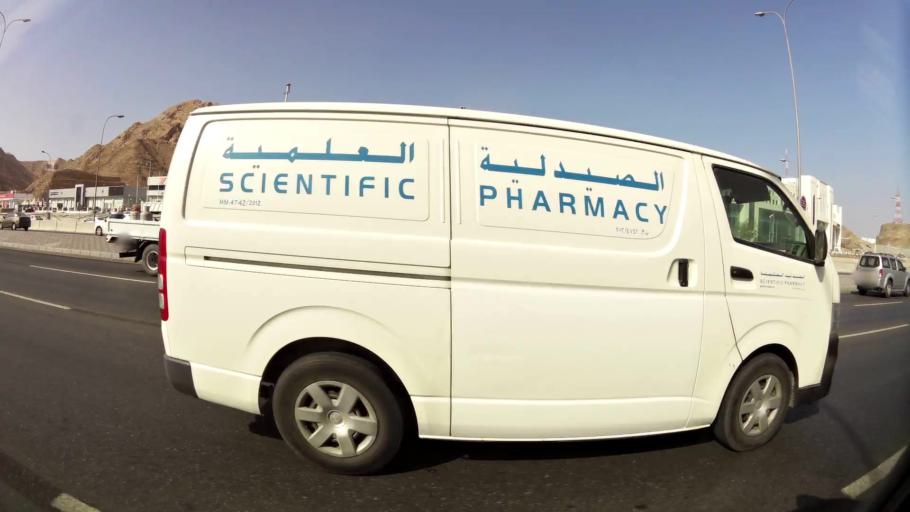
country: OM
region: Muhafazat Masqat
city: Muscat
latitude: 23.5947
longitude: 58.5217
